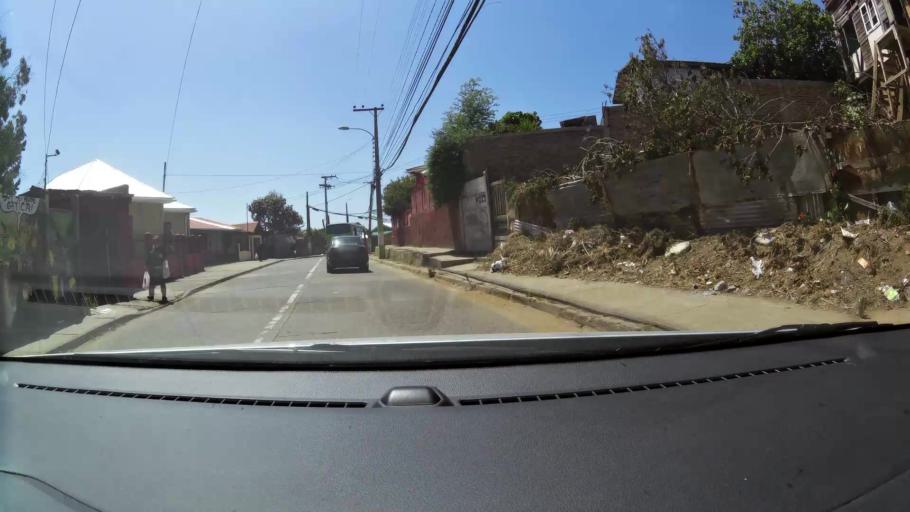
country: CL
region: Valparaiso
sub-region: Provincia de Valparaiso
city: Valparaiso
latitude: -33.0362
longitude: -71.6452
